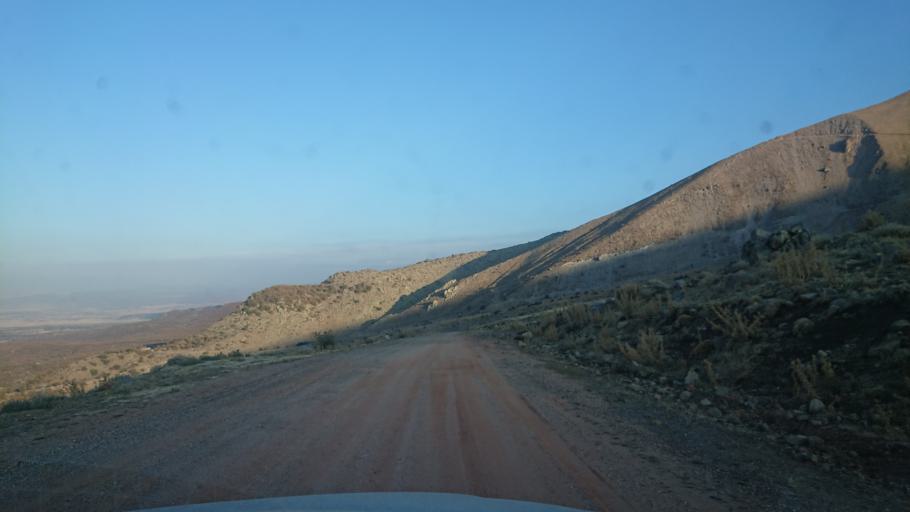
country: TR
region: Aksaray
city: Taspinar
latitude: 38.1612
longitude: 34.1751
